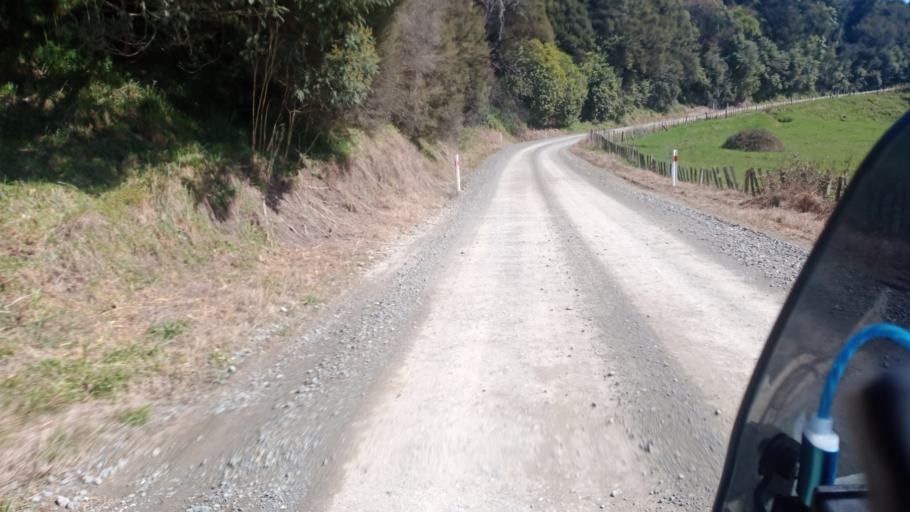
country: NZ
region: Gisborne
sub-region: Gisborne District
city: Gisborne
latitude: -37.9897
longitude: 178.2873
